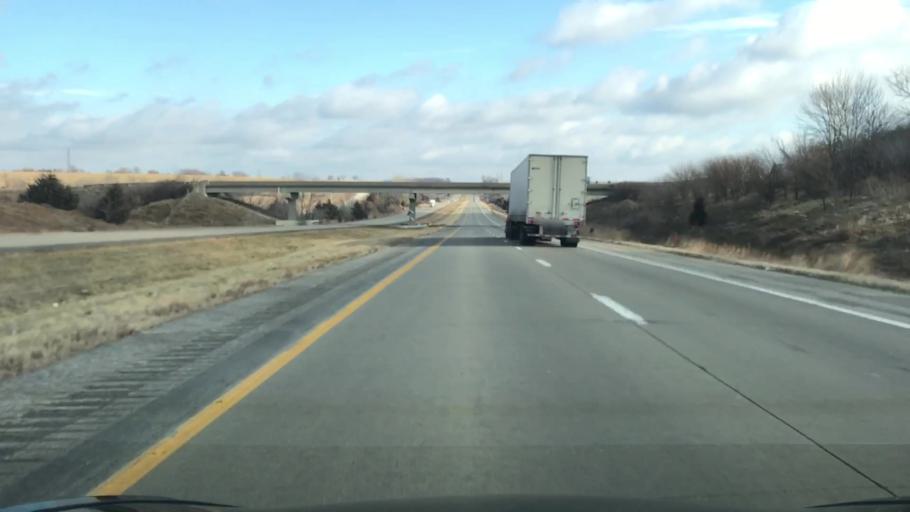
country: US
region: Iowa
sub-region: Cass County
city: Atlantic
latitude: 41.4971
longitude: -94.9133
